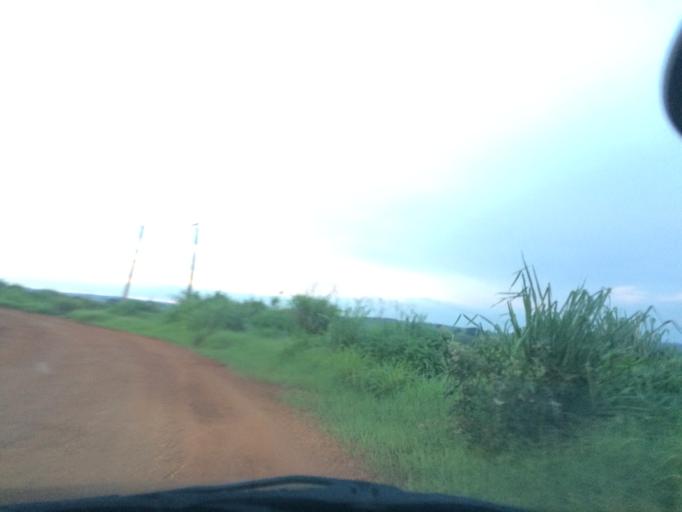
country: BR
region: Sao Paulo
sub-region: Tambau
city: Tambau
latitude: -21.7000
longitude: -47.2152
